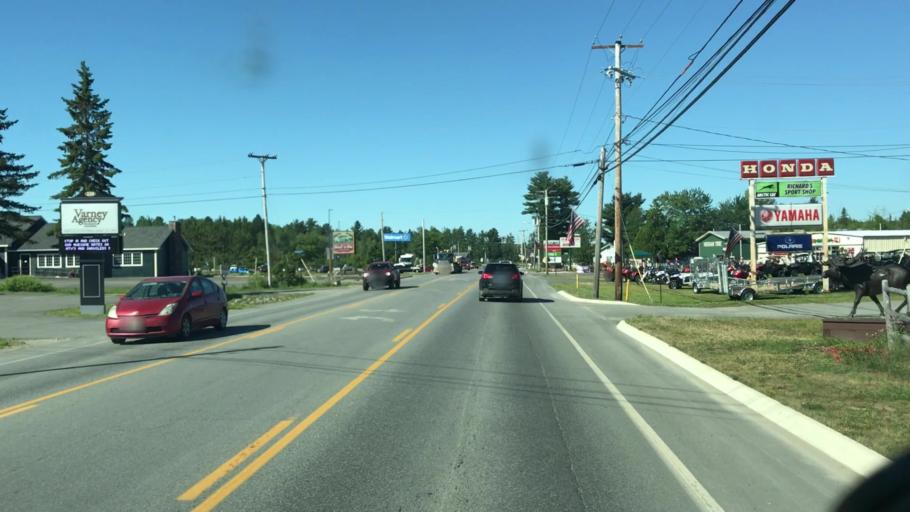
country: US
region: Maine
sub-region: Penobscot County
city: Lincoln
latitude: 45.3581
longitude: -68.5245
